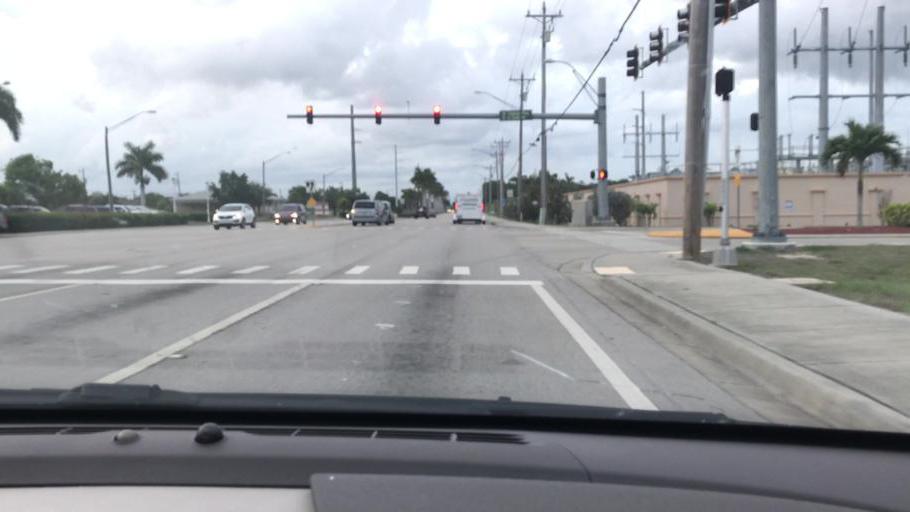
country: US
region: Florida
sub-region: Lee County
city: Cape Coral
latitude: 26.6226
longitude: -81.9742
